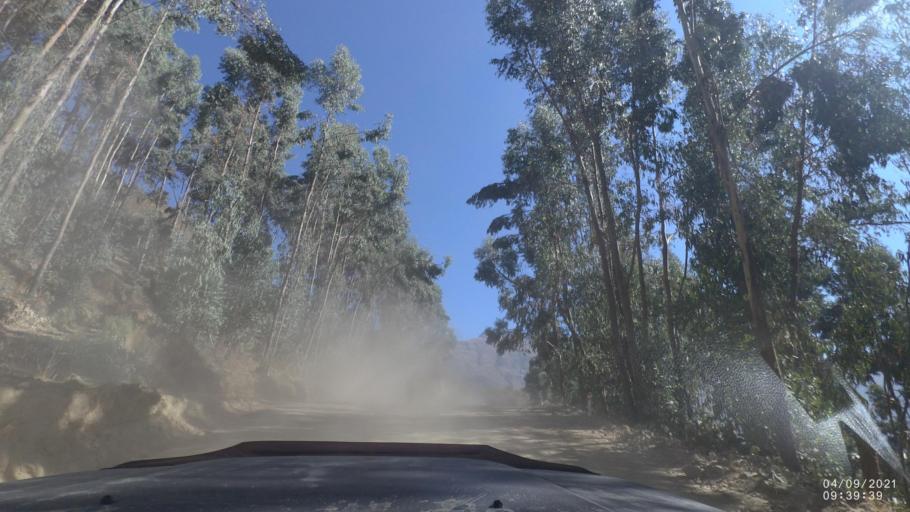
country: BO
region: Cochabamba
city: Sipe Sipe
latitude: -17.3453
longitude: -66.3856
